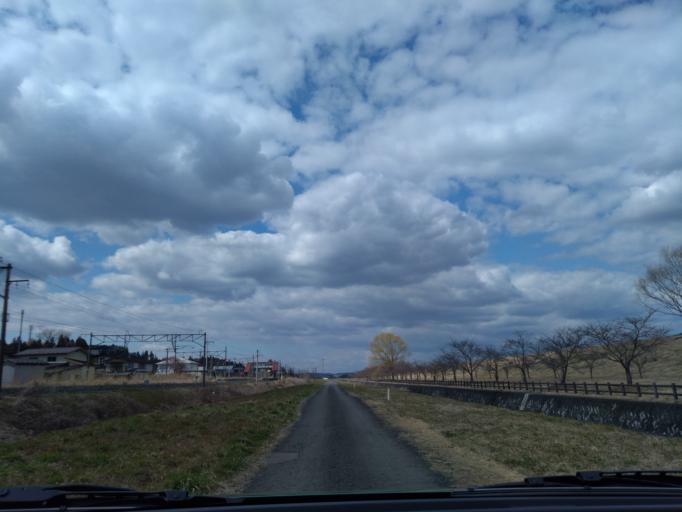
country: JP
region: Iwate
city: Ichinoseki
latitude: 38.9493
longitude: 141.1331
